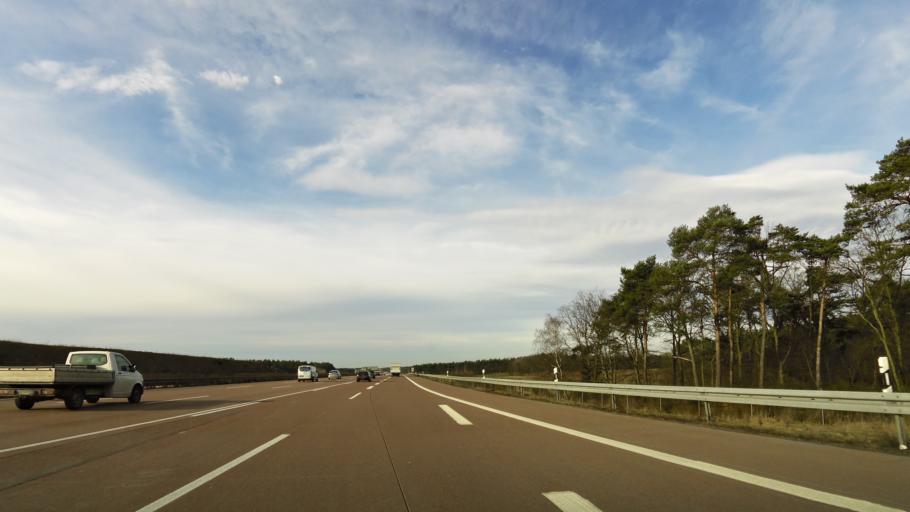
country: DE
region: Brandenburg
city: Michendorf
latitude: 52.3008
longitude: 13.0661
